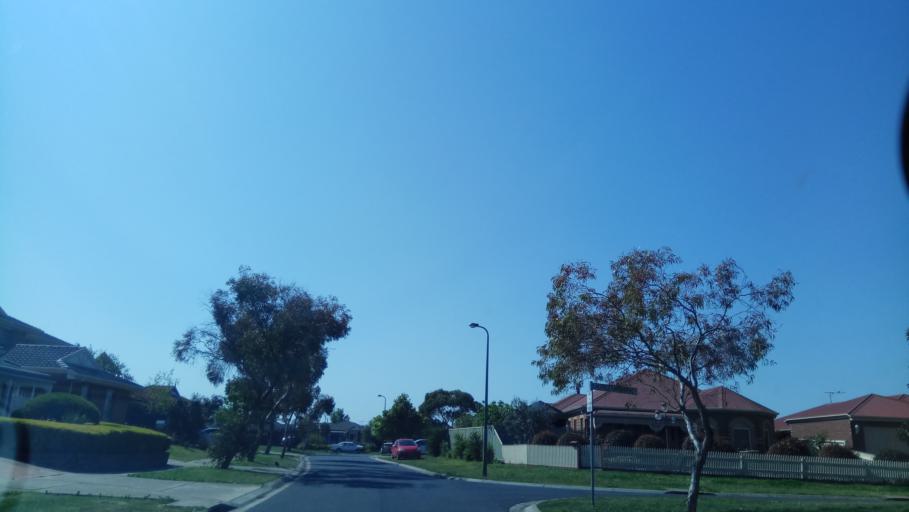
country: AU
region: Victoria
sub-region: Hobsons Bay
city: Altona Meadows
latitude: -37.8846
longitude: 144.7602
